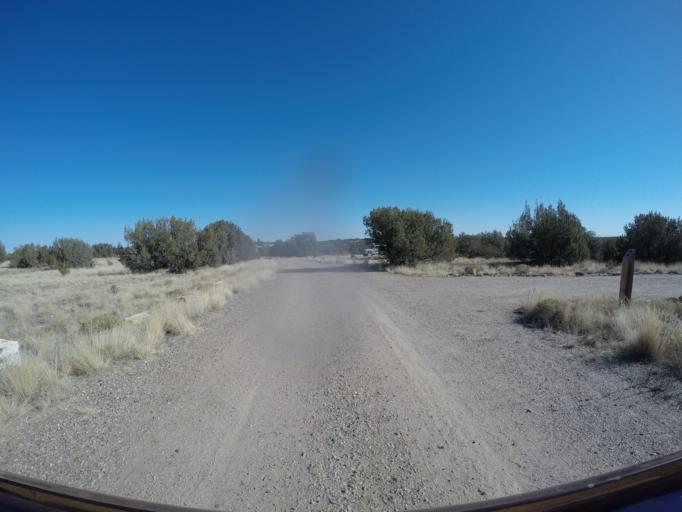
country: US
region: Colorado
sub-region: Otero County
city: La Junta
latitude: 37.6593
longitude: -103.5714
